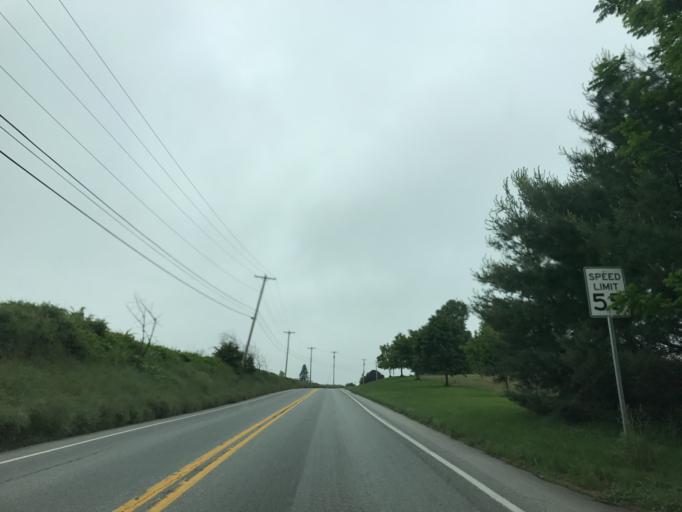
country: US
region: Pennsylvania
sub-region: York County
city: Susquehanna Trails
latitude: 39.8349
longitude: -76.4110
